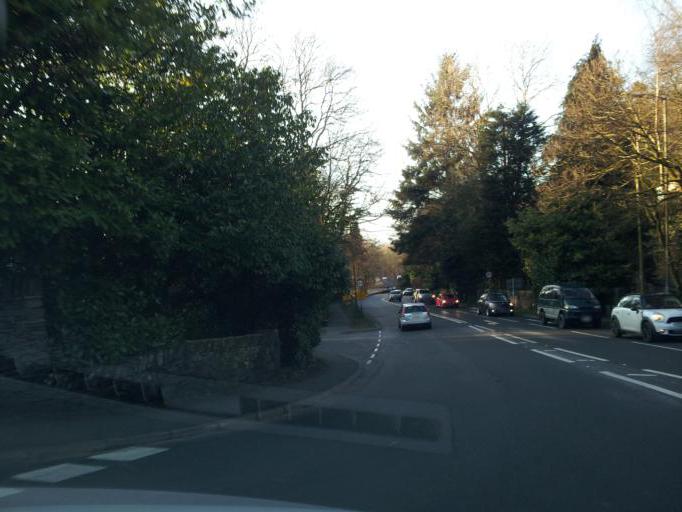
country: GB
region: England
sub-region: Cumbria
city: Windermere
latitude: 54.3860
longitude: -2.9155
